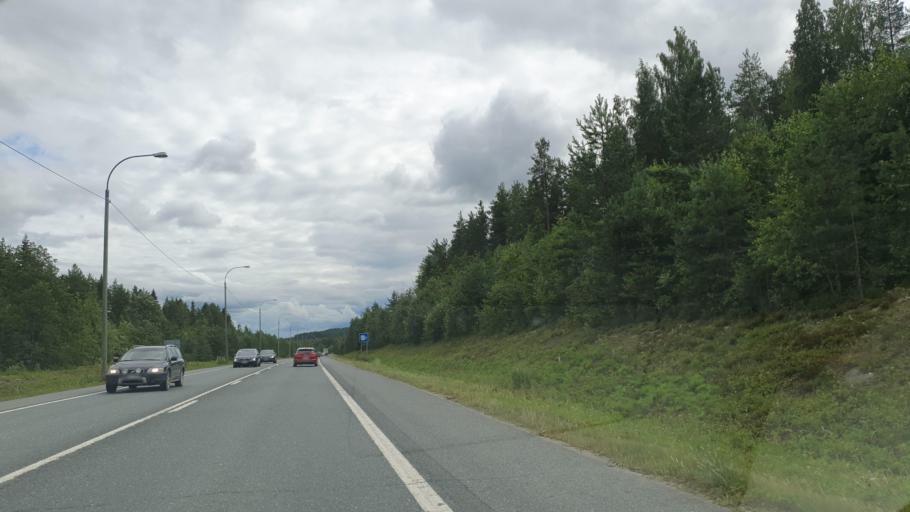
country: FI
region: Northern Savo
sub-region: Ylae-Savo
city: Iisalmi
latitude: 63.5825
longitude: 27.2327
